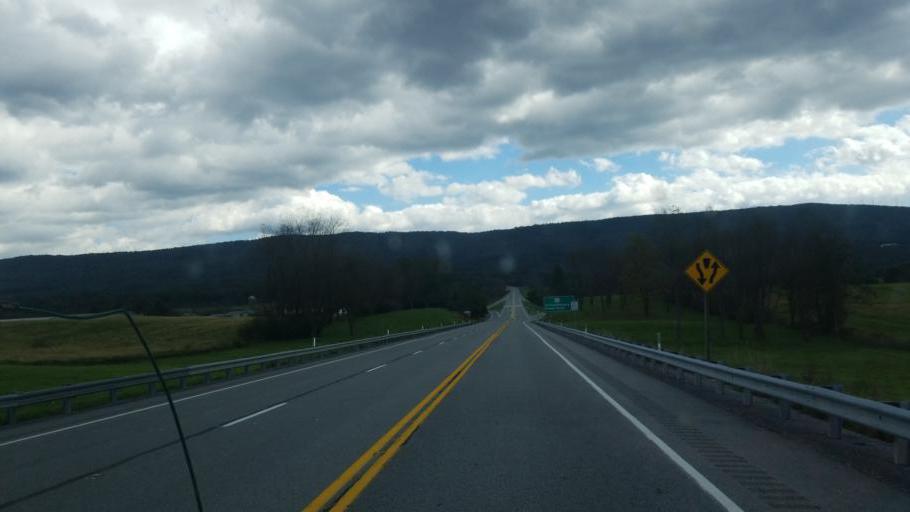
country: US
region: Pennsylvania
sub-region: Fulton County
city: McConnellsburg
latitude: 39.9440
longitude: -78.0016
